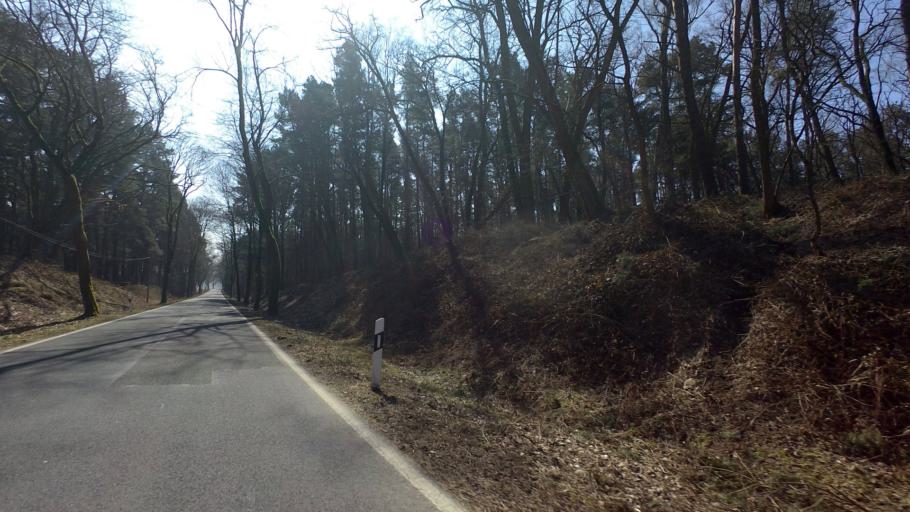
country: DE
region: Brandenburg
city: Wiesenburg
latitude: 52.0322
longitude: 12.5206
